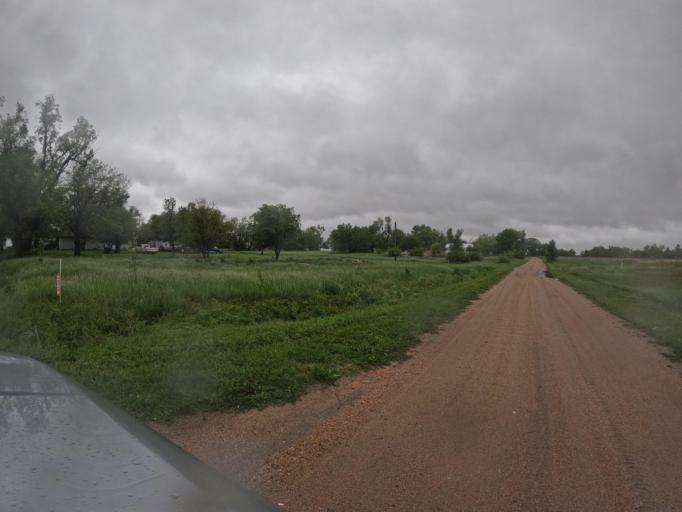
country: US
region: Nebraska
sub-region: Clay County
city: Harvard
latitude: 40.6163
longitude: -98.0987
